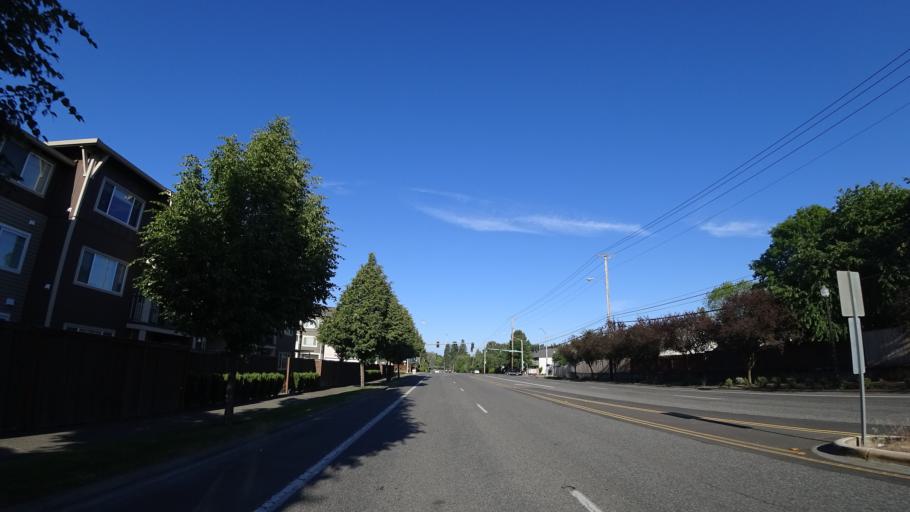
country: US
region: Oregon
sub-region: Washington County
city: Aloha
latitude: 45.5151
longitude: -122.8848
